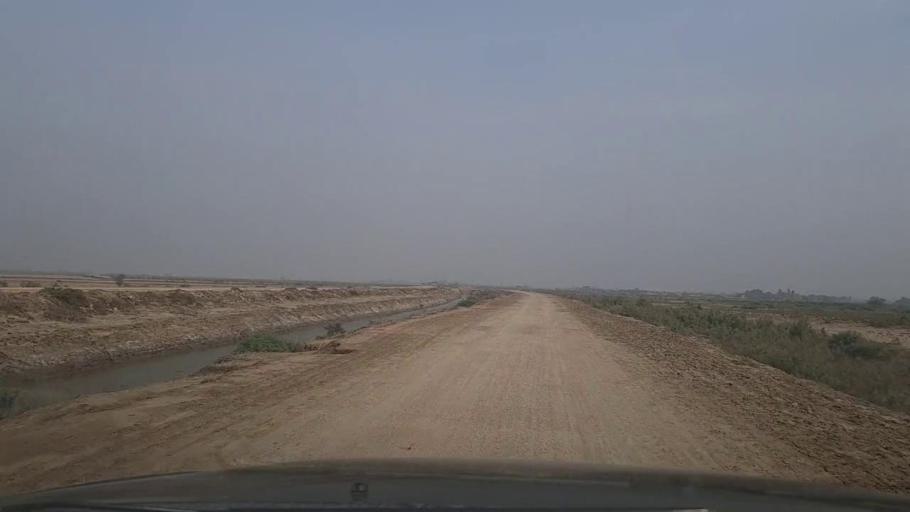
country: PK
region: Sindh
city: Mirpur Sakro
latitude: 24.5324
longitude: 67.7807
